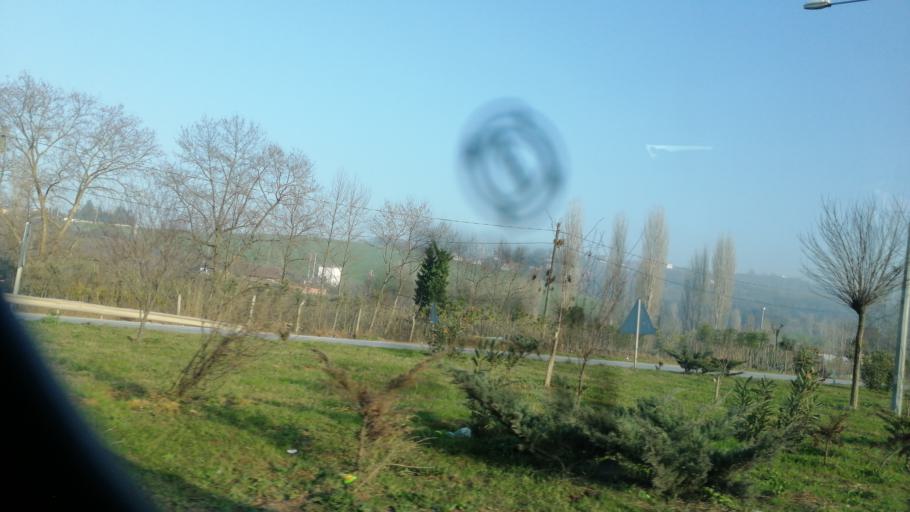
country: TR
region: Yalova
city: Yalova
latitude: 40.6210
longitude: 29.2711
